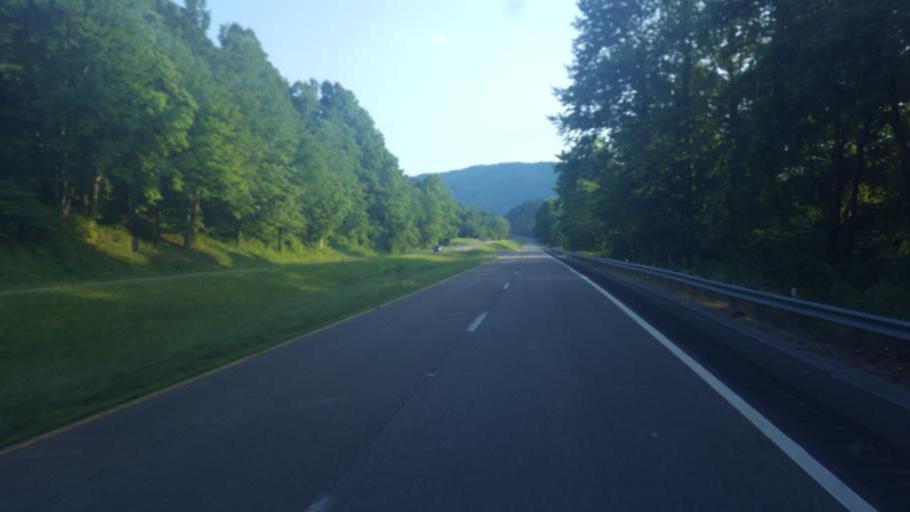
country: US
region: Virginia
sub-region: Wise County
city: Big Stone Gap
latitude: 36.7864
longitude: -82.8165
